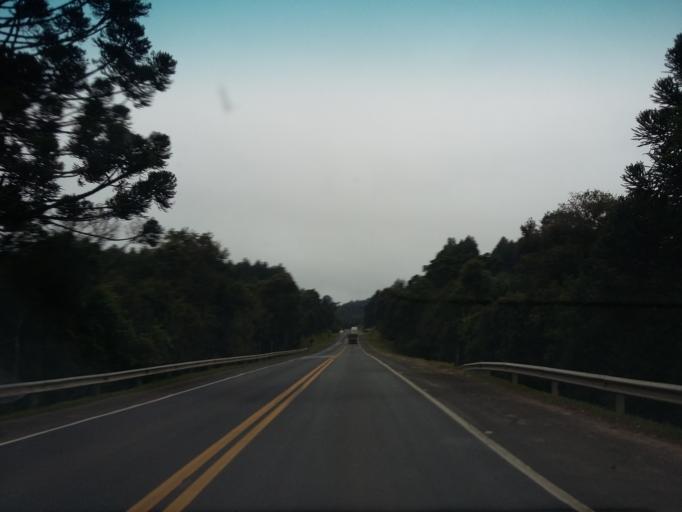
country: BR
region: Santa Catarina
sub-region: Santa Cecilia
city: Santa Cecilia
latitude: -26.6185
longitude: -50.2365
